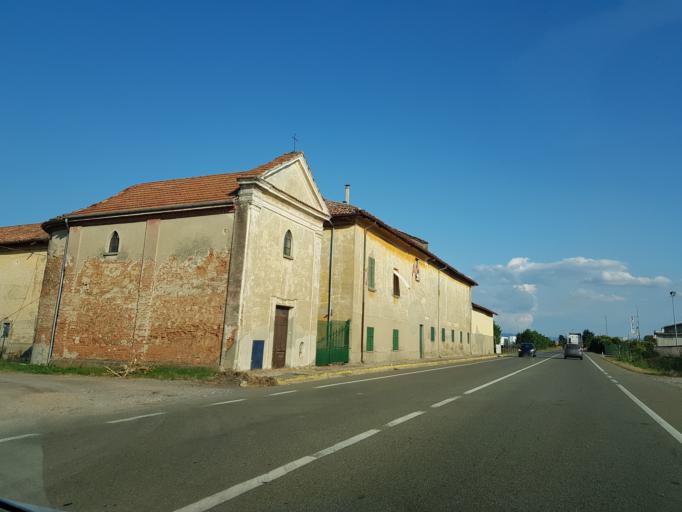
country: IT
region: Piedmont
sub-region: Provincia di Alessandria
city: Mandrogne
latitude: 44.8430
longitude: 8.7278
